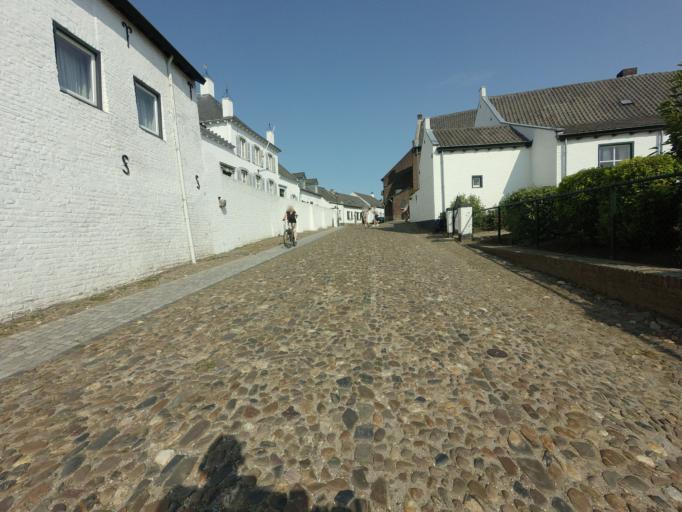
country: NL
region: Limburg
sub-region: Gemeente Maasgouw
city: Maasbracht
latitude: 51.1605
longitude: 5.8390
